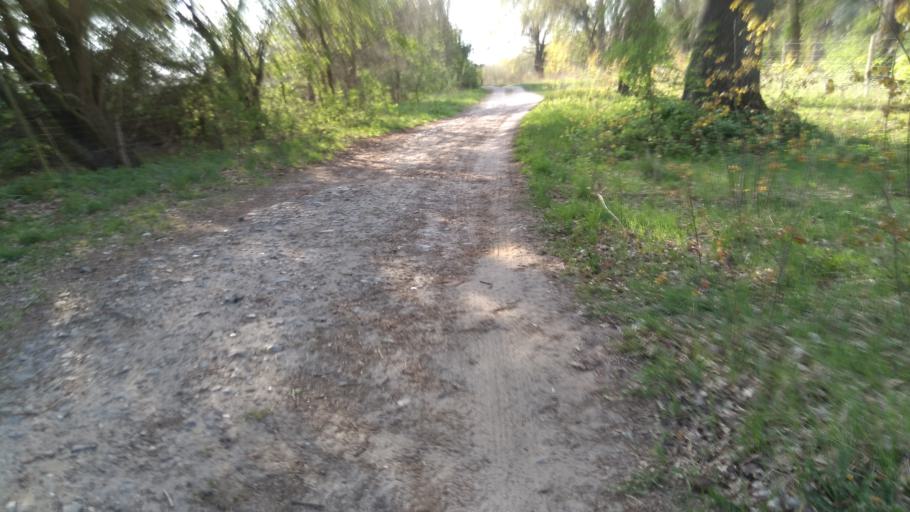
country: DE
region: Lower Saxony
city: Buxtehude
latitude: 53.4392
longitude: 9.6663
